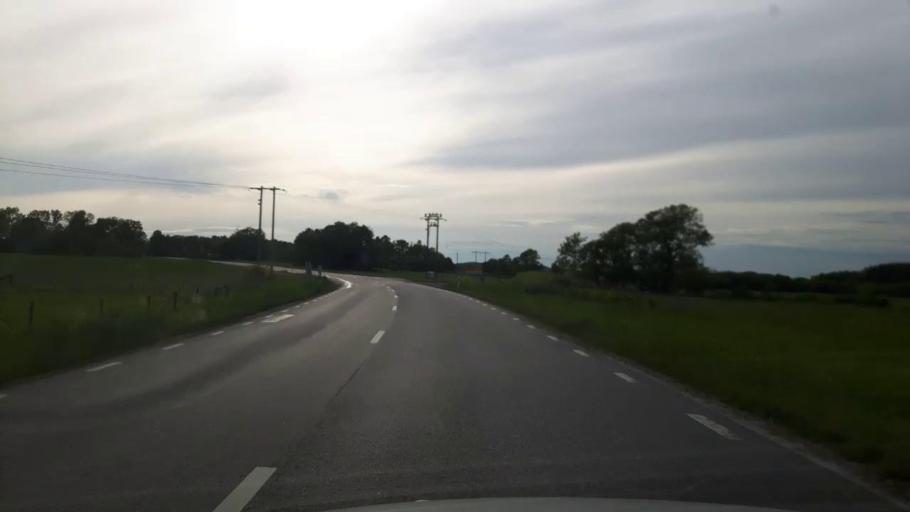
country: SE
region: Uppsala
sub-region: Enkopings Kommun
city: Orsundsbro
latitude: 59.6542
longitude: 17.4054
